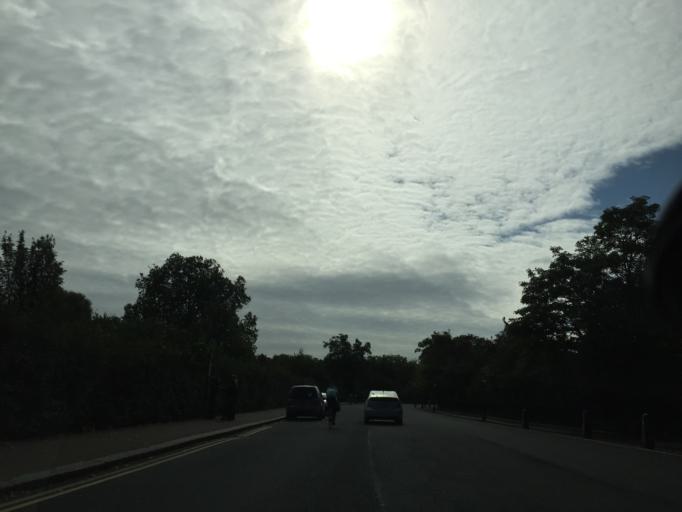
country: GB
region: England
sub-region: Greater London
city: Camden Town
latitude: 51.5272
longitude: -0.1613
